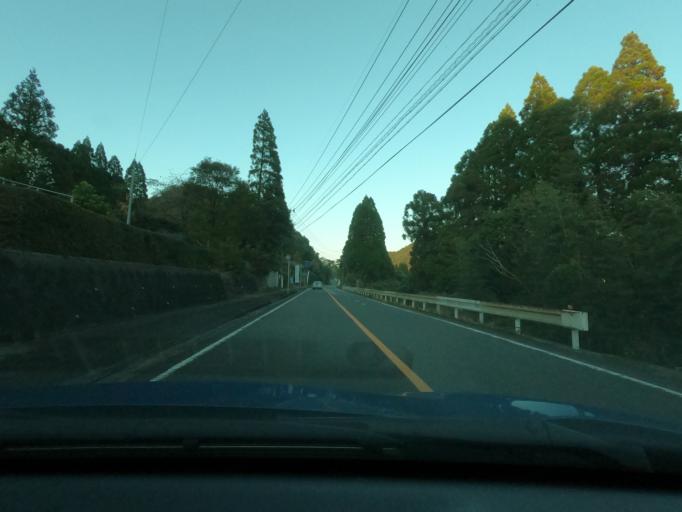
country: JP
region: Kagoshima
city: Satsumasendai
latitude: 31.7972
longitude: 130.4777
